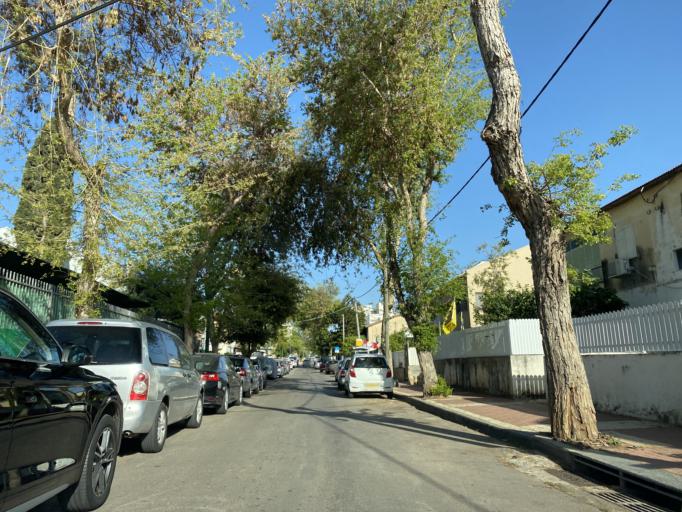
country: IL
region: Central District
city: Kfar Saba
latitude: 32.1810
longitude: 34.9173
